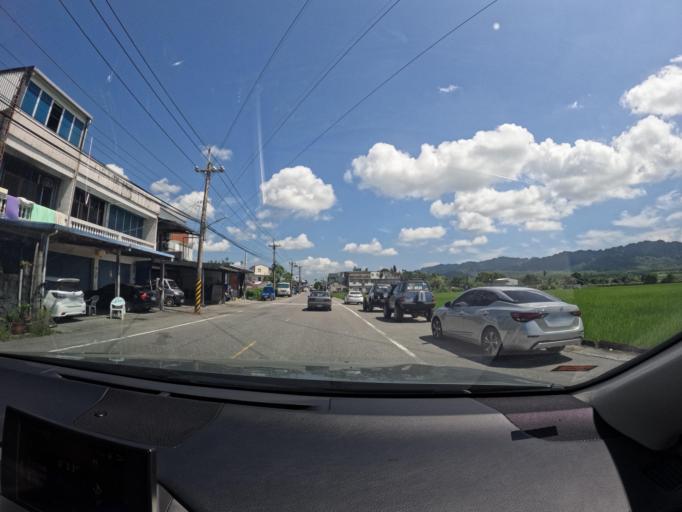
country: TW
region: Taiwan
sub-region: Hualien
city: Hualian
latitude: 23.5781
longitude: 121.3773
